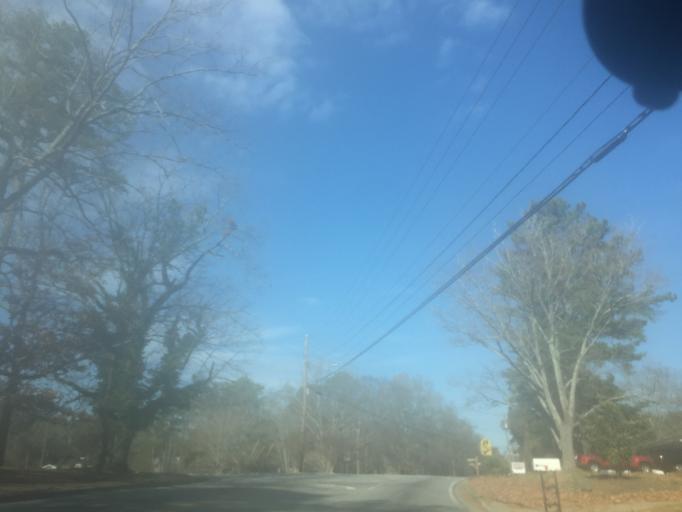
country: US
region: Georgia
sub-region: Clayton County
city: Riverdale
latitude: 33.5634
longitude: -84.4169
